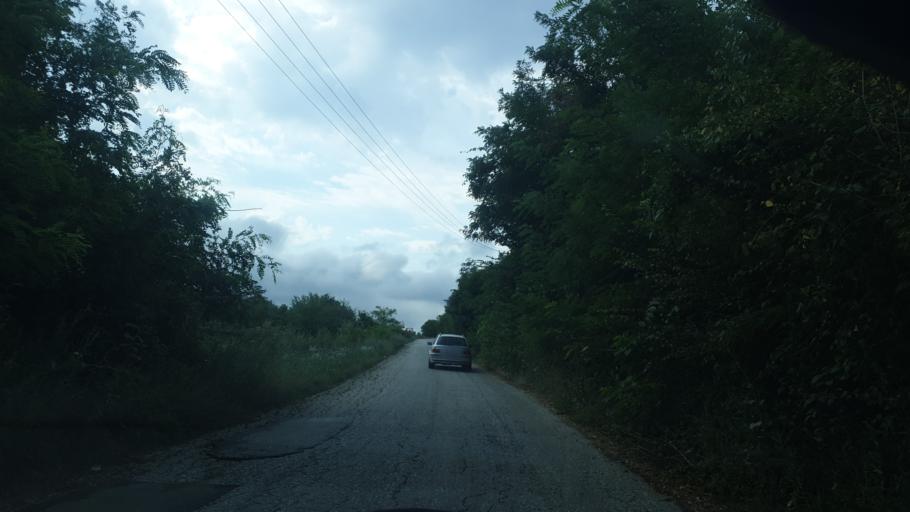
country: RS
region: Central Serbia
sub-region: Sumadijski Okrug
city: Kragujevac
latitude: 44.1015
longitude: 20.7802
